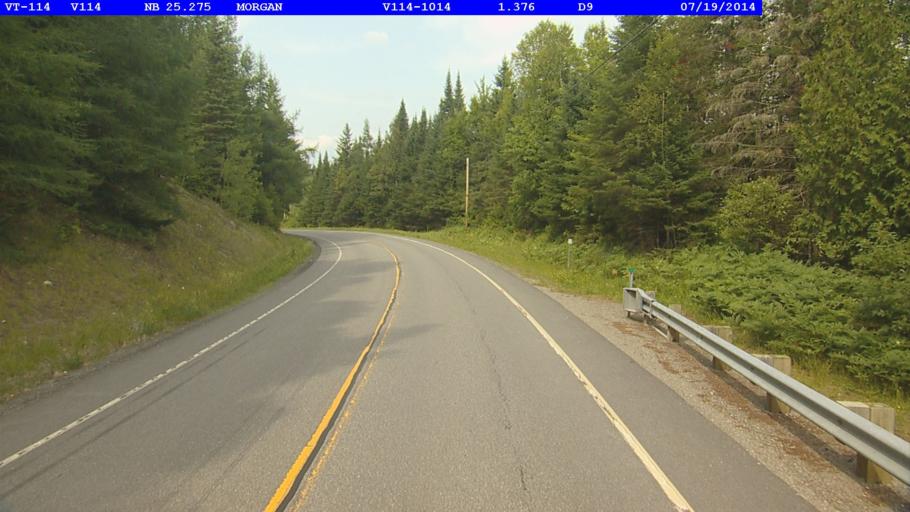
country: CA
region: Quebec
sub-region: Estrie
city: Coaticook
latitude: 44.8659
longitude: -71.9063
